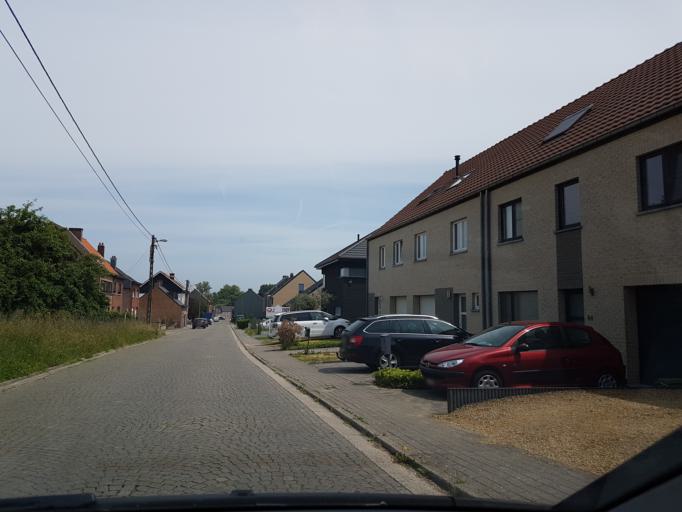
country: BE
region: Flanders
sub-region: Provincie Oost-Vlaanderen
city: Denderleeuw
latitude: 50.9173
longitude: 4.1053
